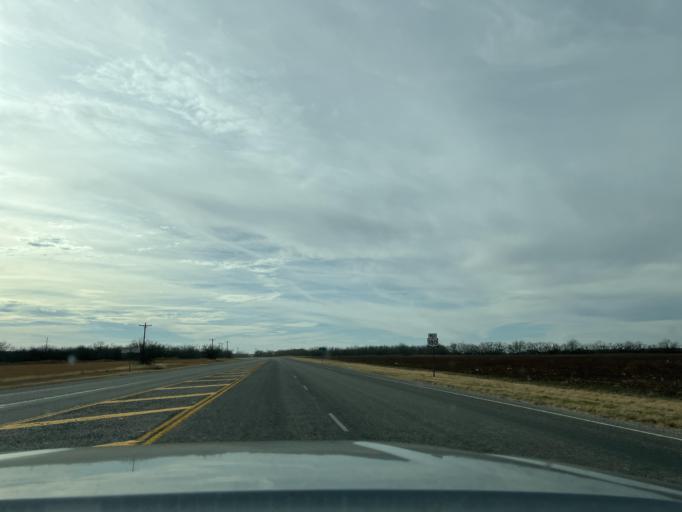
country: US
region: Texas
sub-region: Jones County
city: Stamford
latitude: 32.7662
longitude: -99.5923
